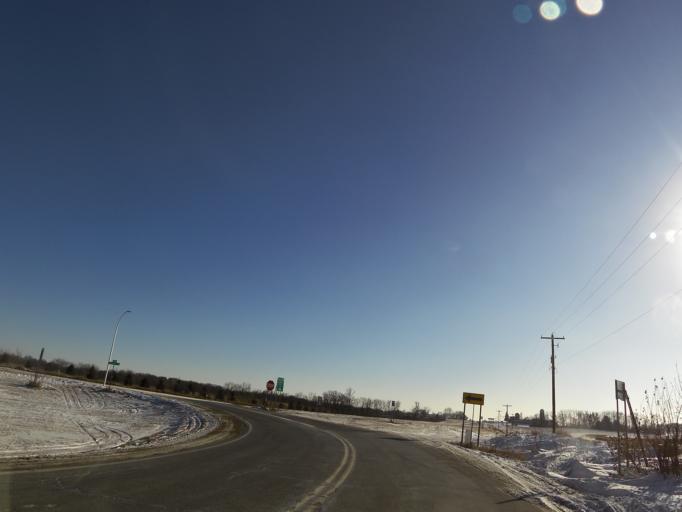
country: US
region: Minnesota
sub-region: Scott County
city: Prior Lake
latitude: 44.6878
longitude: -93.5010
